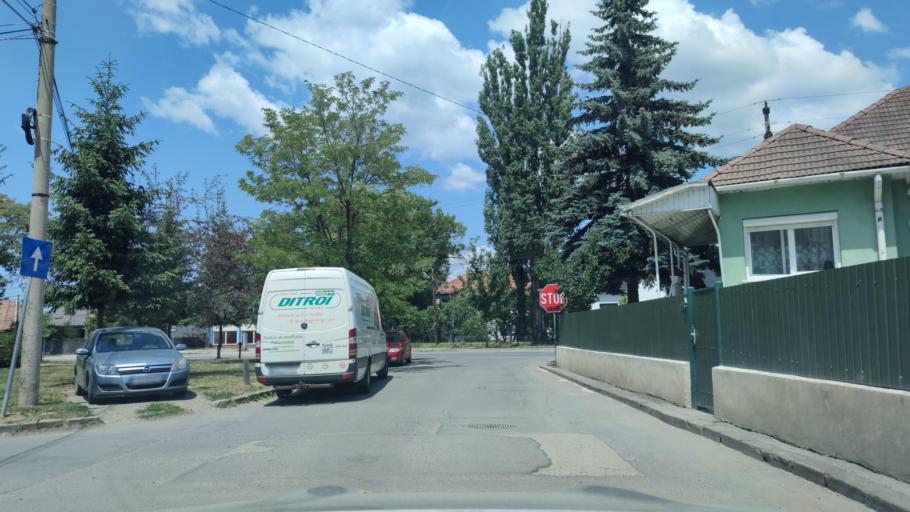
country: RO
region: Harghita
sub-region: Municipiul Gheorgheni
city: Gheorgheni
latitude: 46.7234
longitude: 25.5948
